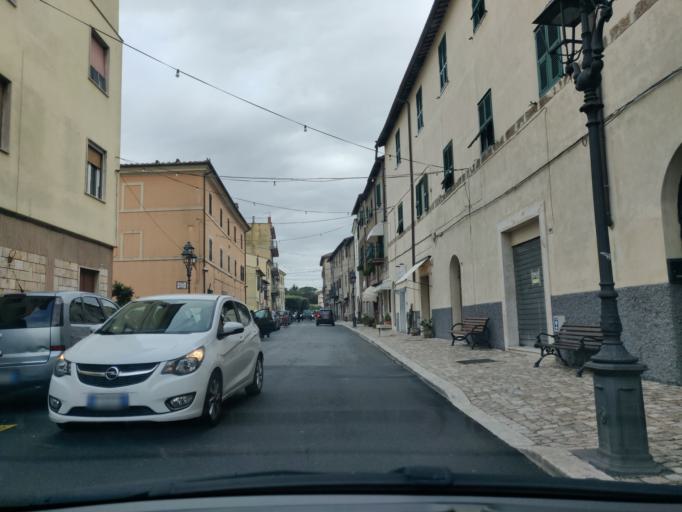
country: IT
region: Latium
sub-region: Citta metropolitana di Roma Capitale
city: Tolfa
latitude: 42.1512
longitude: 11.9397
